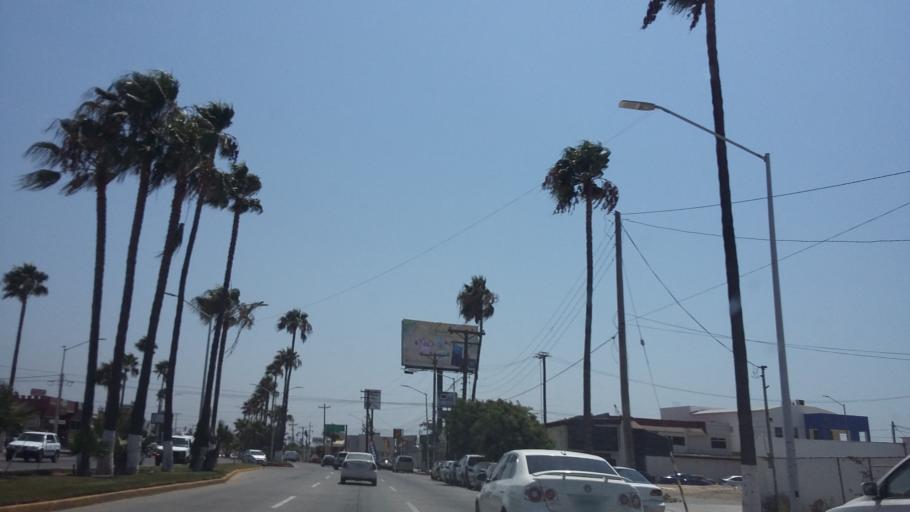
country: MX
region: Baja California
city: Ensenada
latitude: 31.8515
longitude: -116.6158
